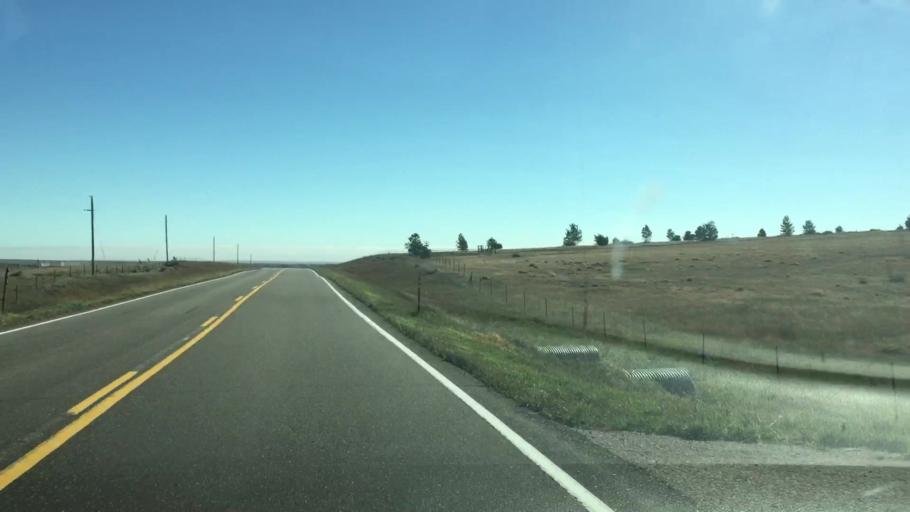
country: US
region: Colorado
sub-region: Lincoln County
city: Limon
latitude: 39.2881
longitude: -103.9490
